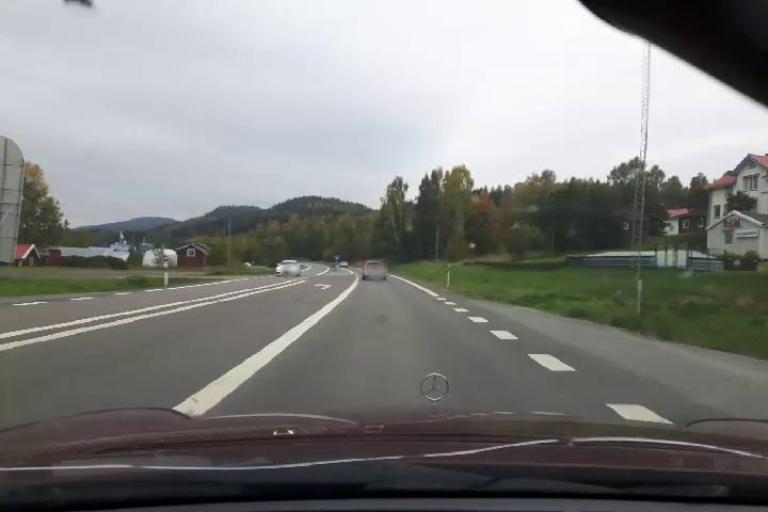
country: SE
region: Vaesternorrland
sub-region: Kramfors Kommun
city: Nordingra
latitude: 63.0485
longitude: 18.3258
